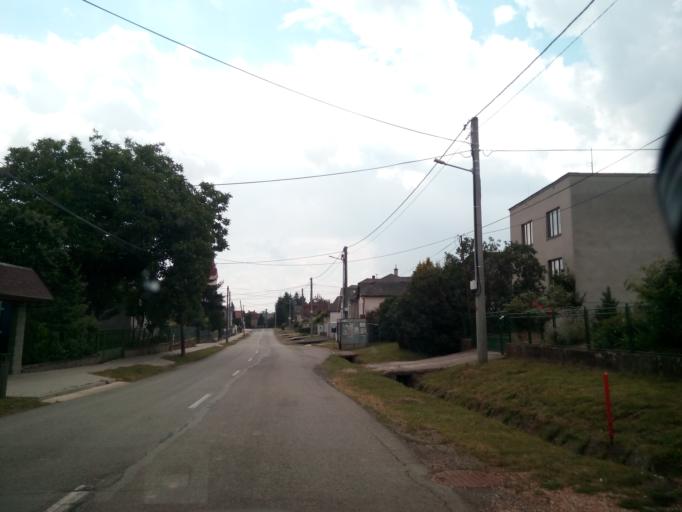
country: SK
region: Kosicky
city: Secovce
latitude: 48.5839
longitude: 21.5679
